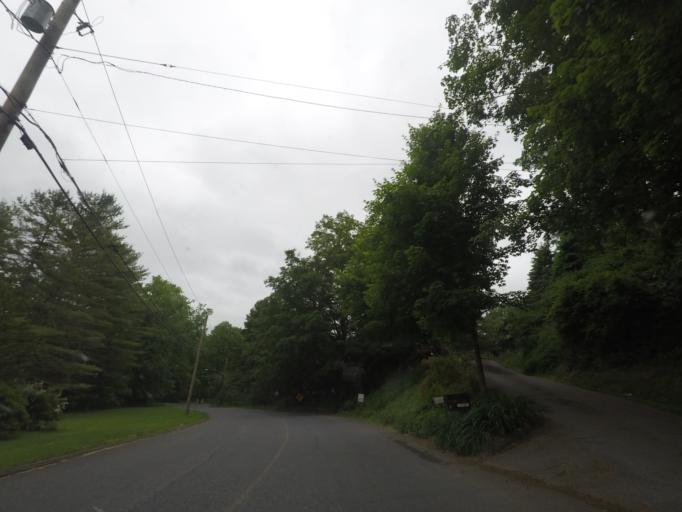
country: US
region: Connecticut
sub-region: Litchfield County
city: Canaan
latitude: 41.9344
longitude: -73.3916
